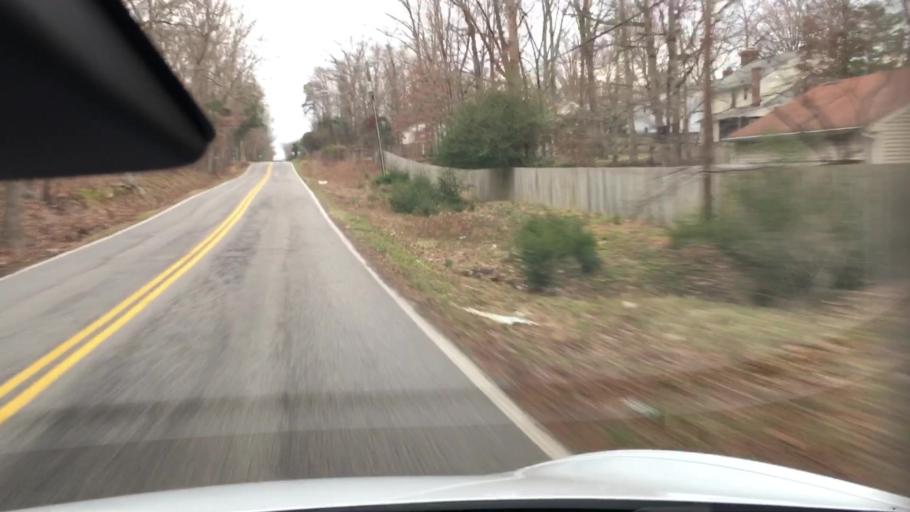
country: US
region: Virginia
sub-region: Chesterfield County
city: Bon Air
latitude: 37.5194
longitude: -77.5733
